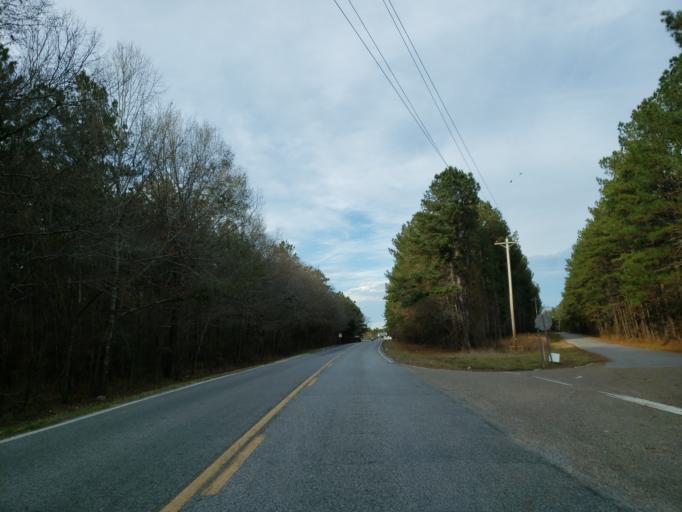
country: US
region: Mississippi
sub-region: Wayne County
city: Waynesboro
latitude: 31.8397
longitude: -88.6881
